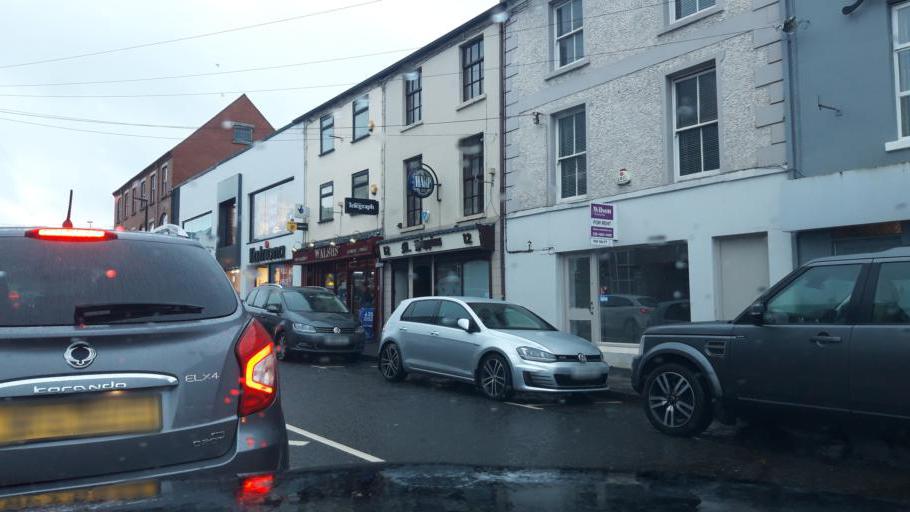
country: GB
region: Northern Ireland
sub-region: Banbridge District
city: Banbridge
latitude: 54.3490
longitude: -6.2712
